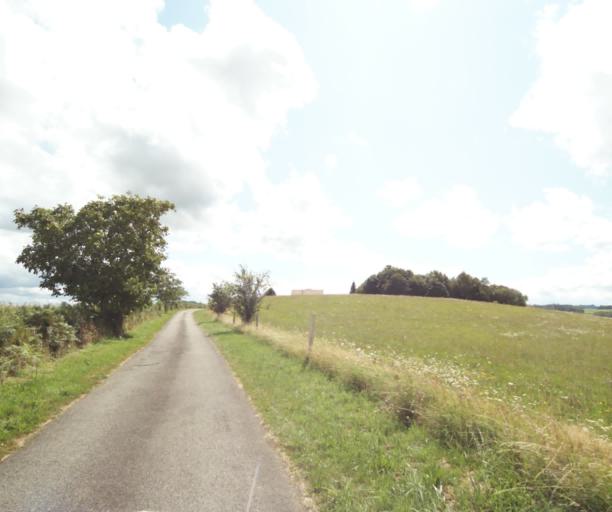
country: FR
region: Limousin
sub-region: Departement de la Correze
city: Sainte-Fortunade
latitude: 45.1755
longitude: 1.8279
